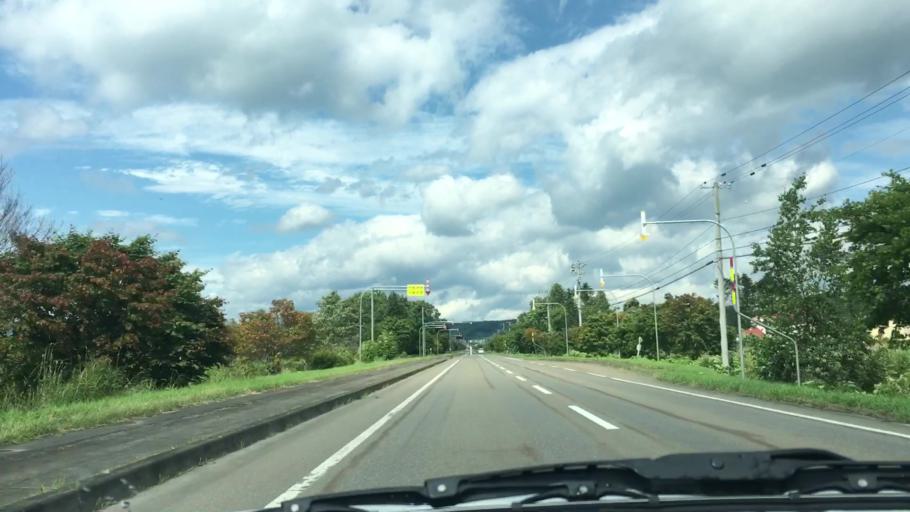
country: JP
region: Hokkaido
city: Otofuke
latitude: 43.2931
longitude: 143.3087
